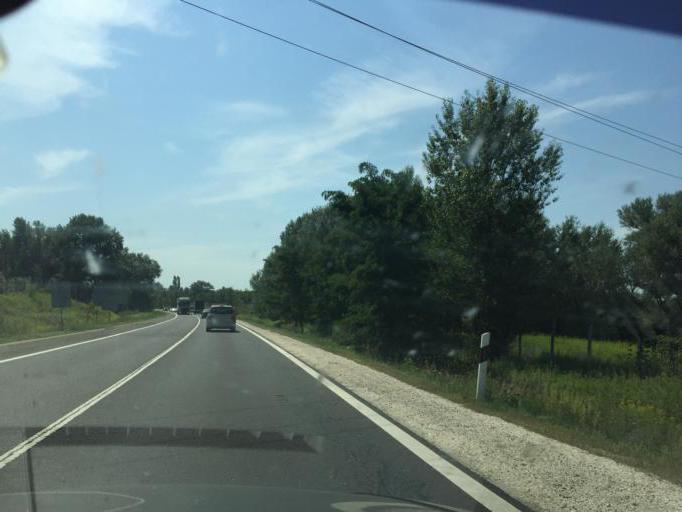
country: HU
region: Pest
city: Szodliget
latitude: 47.7236
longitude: 19.1570
